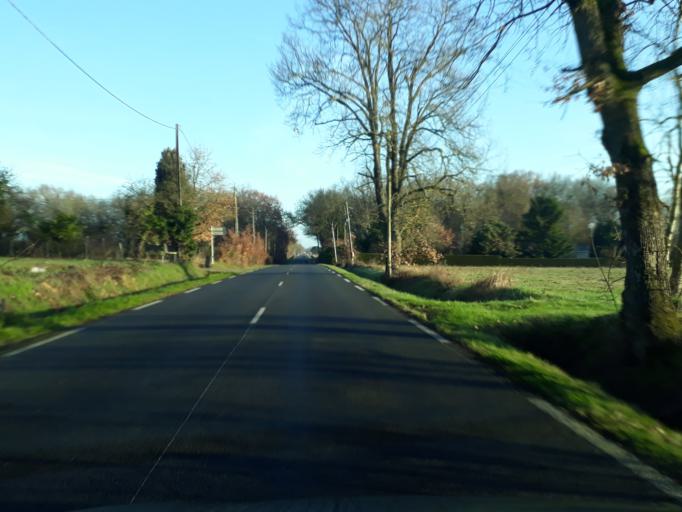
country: FR
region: Midi-Pyrenees
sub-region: Departement de la Haute-Garonne
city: Rieumes
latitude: 43.4300
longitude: 1.1322
